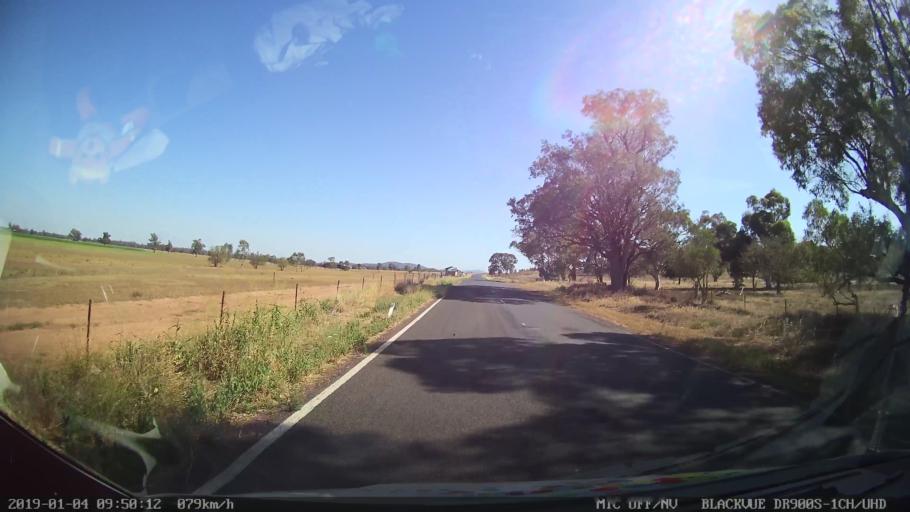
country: AU
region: New South Wales
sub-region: Cabonne
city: Canowindra
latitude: -33.5870
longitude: 148.4148
